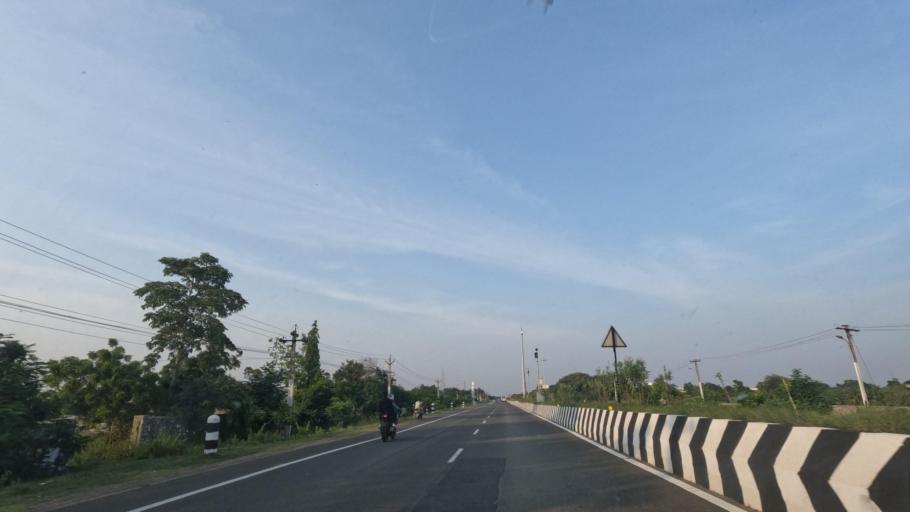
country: IN
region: Tamil Nadu
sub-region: Kancheepuram
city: Mamallapuram
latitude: 12.6963
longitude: 80.2202
